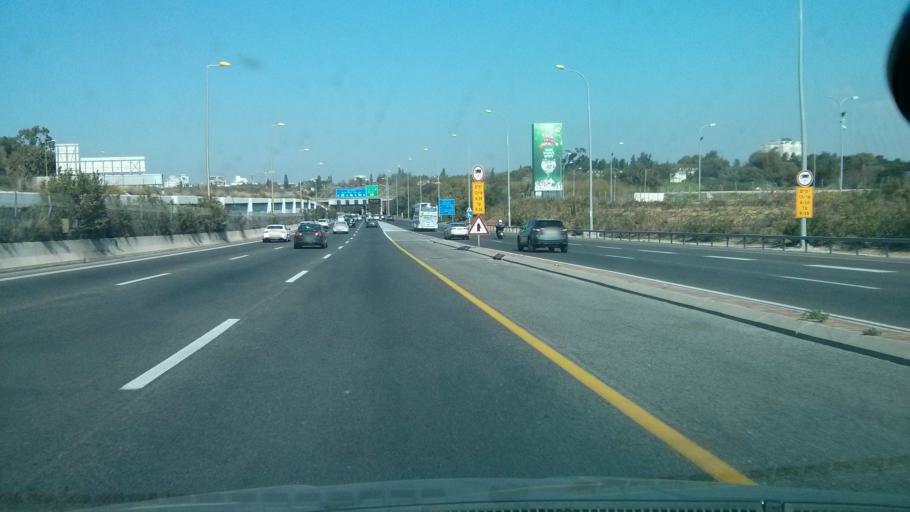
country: IL
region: Tel Aviv
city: Ramat Gan
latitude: 32.1092
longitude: 34.8086
